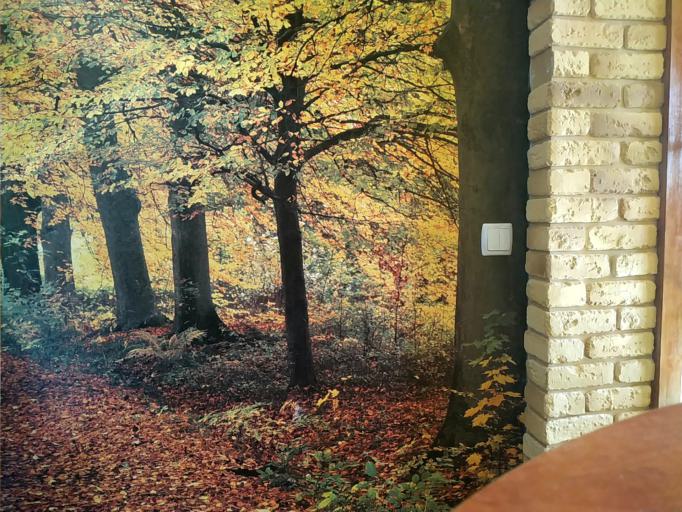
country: RU
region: Jaroslavl
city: Kukoboy
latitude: 58.8588
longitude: 39.7305
